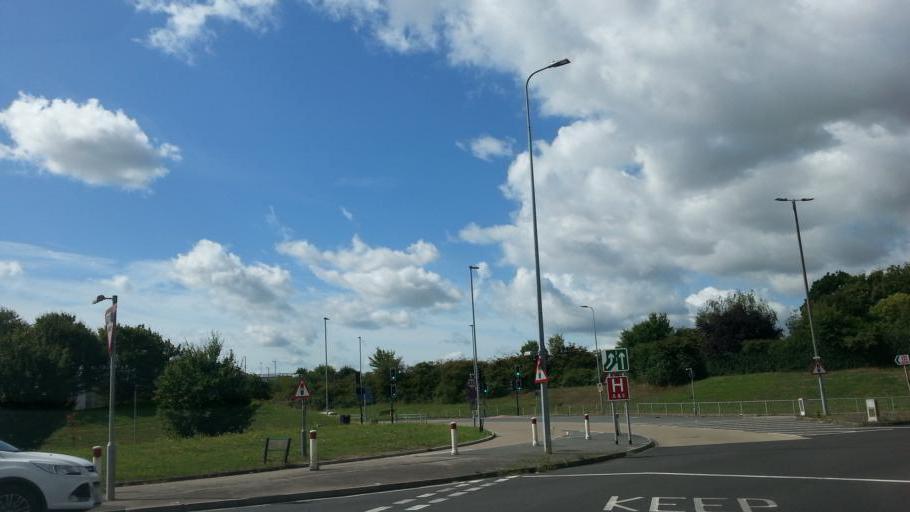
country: GB
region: England
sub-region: Essex
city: Basildon
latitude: 51.5610
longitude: 0.4531
